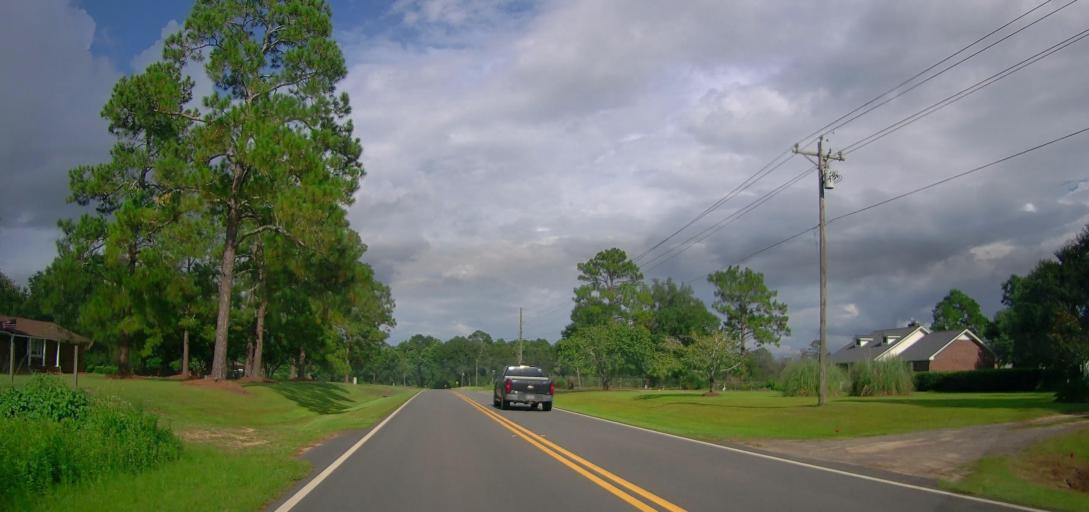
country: US
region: Georgia
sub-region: Coffee County
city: Douglas
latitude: 31.4484
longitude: -82.8722
